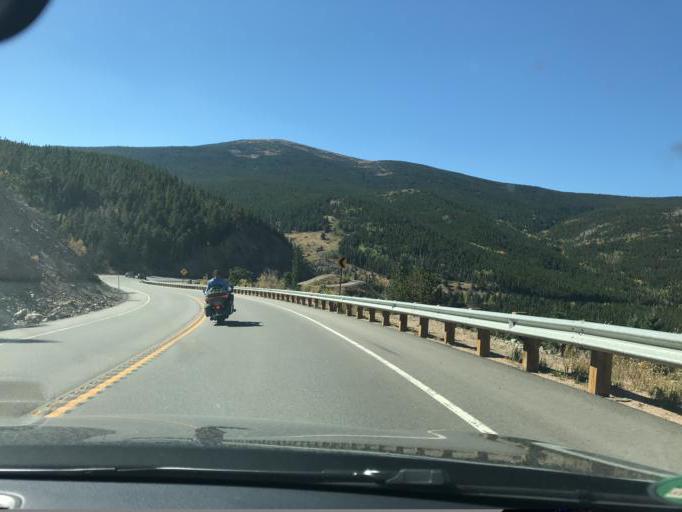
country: US
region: Colorado
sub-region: Boulder County
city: Nederland
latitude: 40.0522
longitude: -105.5166
